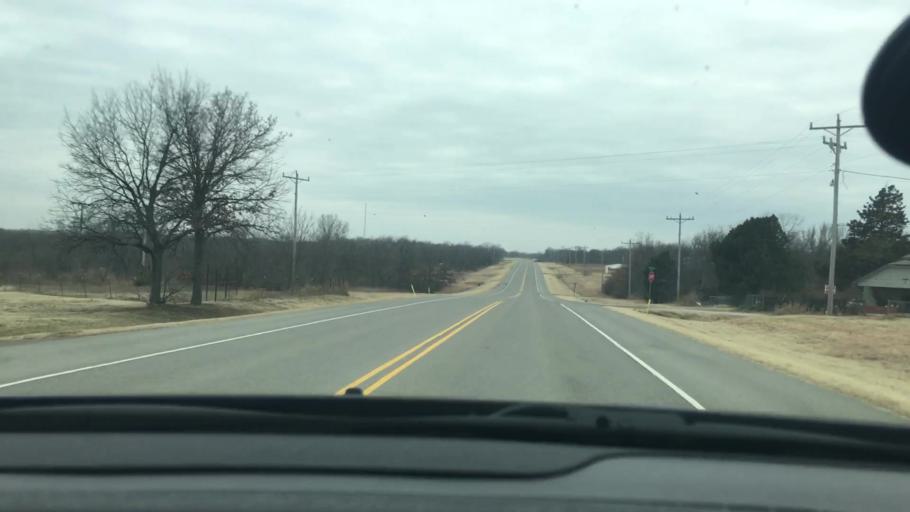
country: US
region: Oklahoma
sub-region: Carter County
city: Healdton
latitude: 34.4818
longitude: -97.4612
